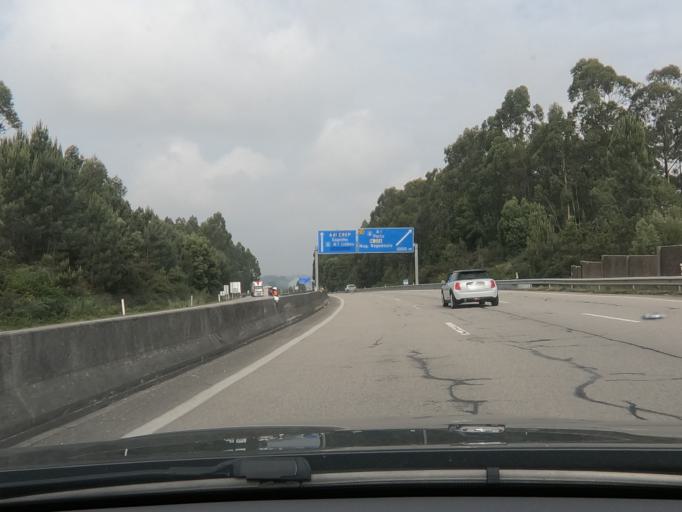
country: PT
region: Aveiro
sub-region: Santa Maria da Feira
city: Lamas
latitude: 41.0100
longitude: -8.5615
